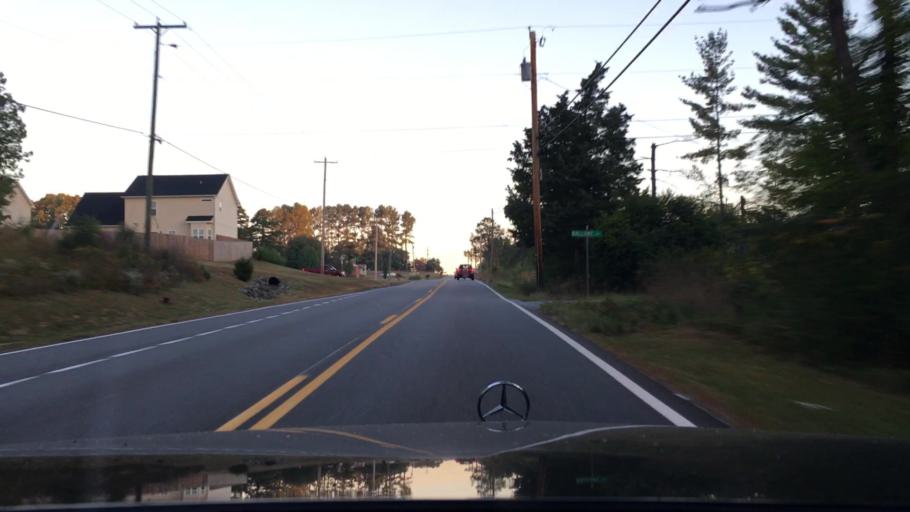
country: US
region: Virginia
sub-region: Campbell County
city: Timberlake
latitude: 37.3063
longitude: -79.2350
